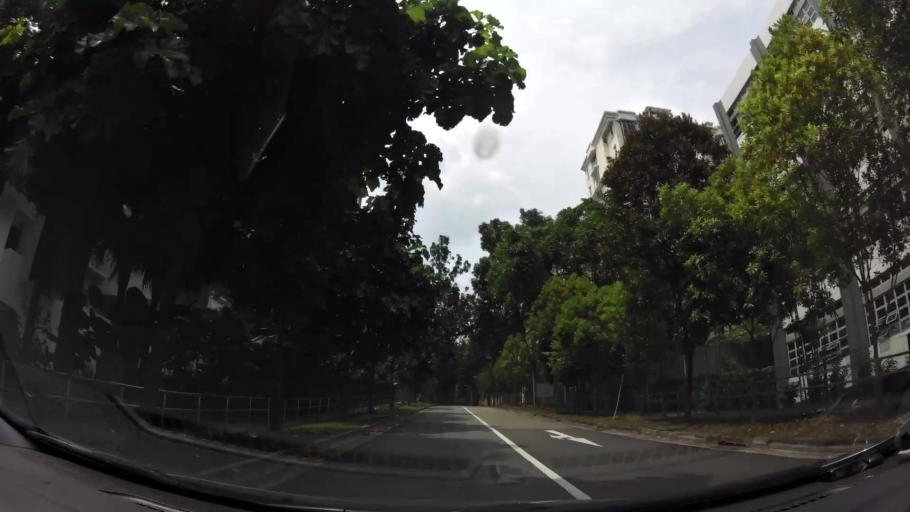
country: MY
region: Johor
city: Johor Bahru
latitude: 1.3566
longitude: 103.7615
